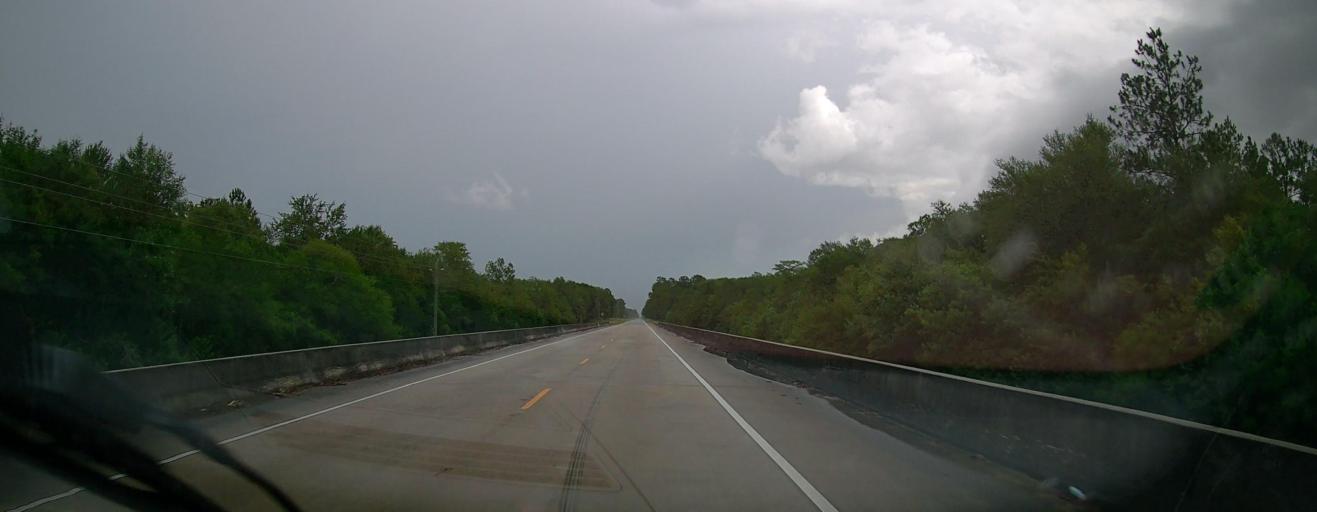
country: US
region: Georgia
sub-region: Brantley County
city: Nahunta
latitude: 31.3440
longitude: -81.9975
